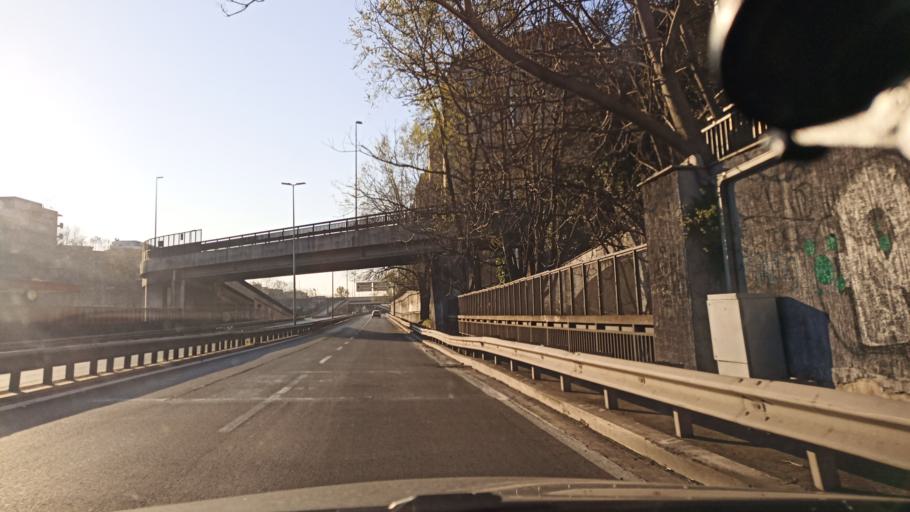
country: IT
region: Latium
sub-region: Citta metropolitana di Roma Capitale
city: Rome
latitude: 41.9326
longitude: 12.5228
